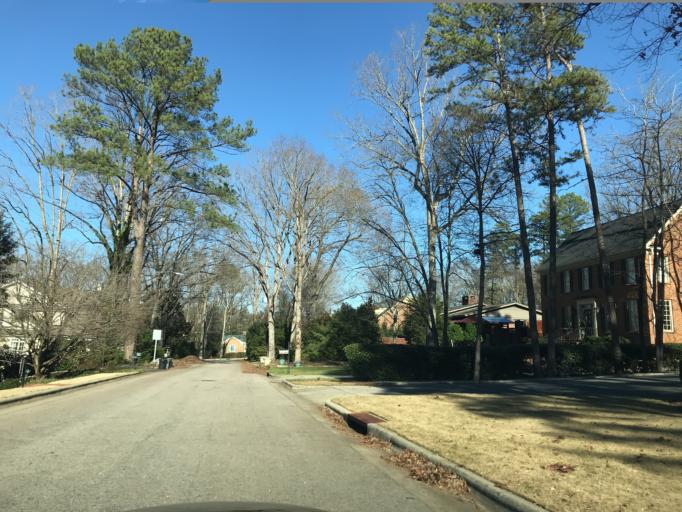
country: US
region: North Carolina
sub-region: Wake County
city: West Raleigh
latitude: 35.8254
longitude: -78.6555
